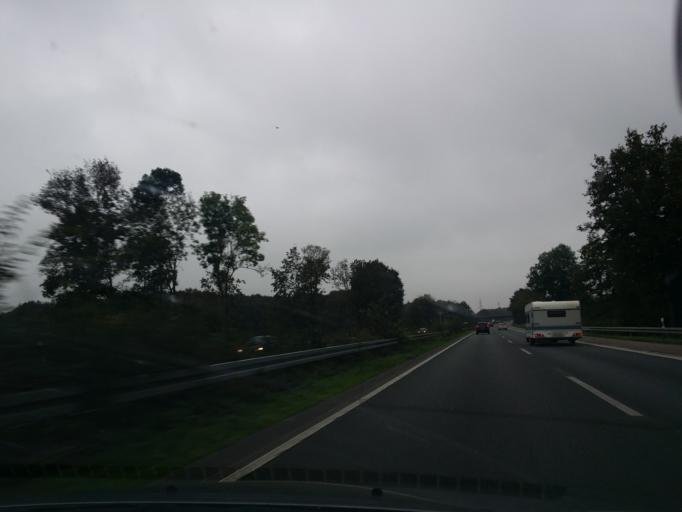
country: DE
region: North Rhine-Westphalia
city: Werne
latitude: 51.6886
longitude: 7.6725
